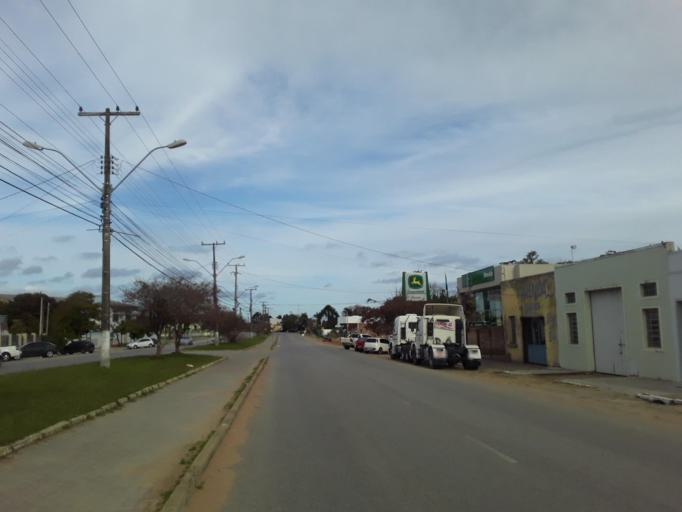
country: BR
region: Rio Grande do Sul
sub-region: Sao Lourenco Do Sul
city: Sao Lourenco do Sul
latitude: -31.3545
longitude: -51.9887
